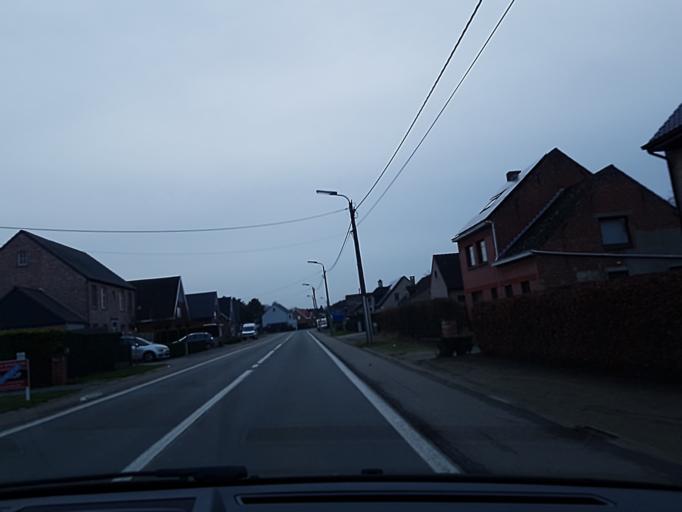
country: BE
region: Flanders
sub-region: Provincie Vlaams-Brabant
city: Keerbergen
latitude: 51.0104
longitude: 4.6488
